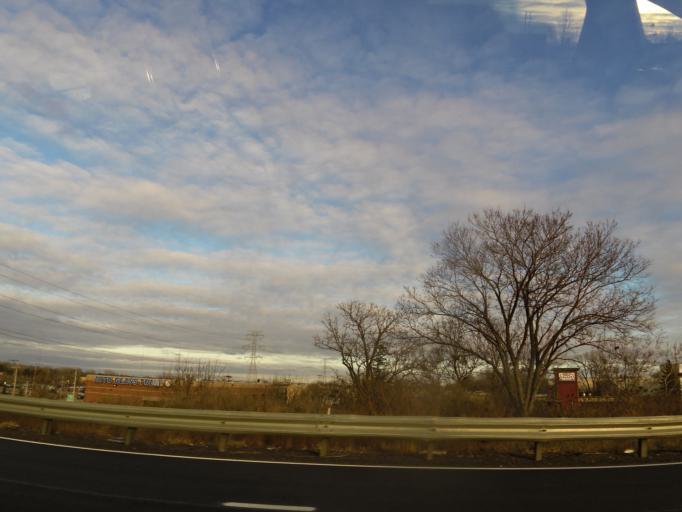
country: US
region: Minnesota
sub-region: Ramsey County
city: Lauderdale
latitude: 45.0189
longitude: -93.1886
